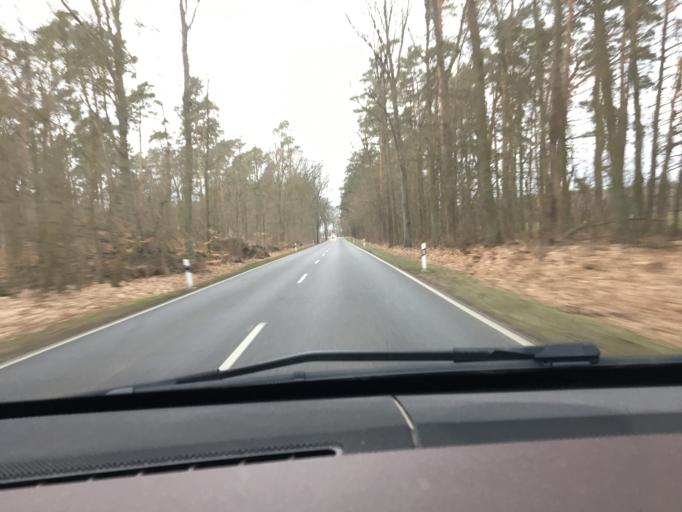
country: DE
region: Brandenburg
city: Liebenwalde
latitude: 52.8753
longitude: 13.4808
